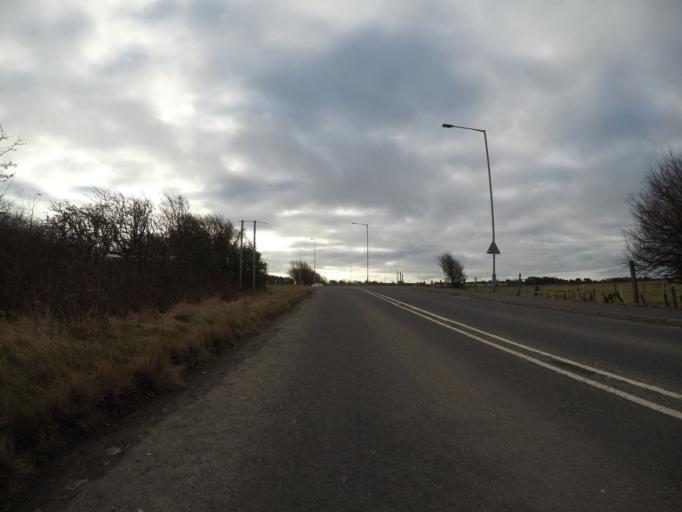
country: GB
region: Scotland
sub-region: North Ayrshire
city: Dreghorn
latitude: 55.5768
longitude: -4.6422
